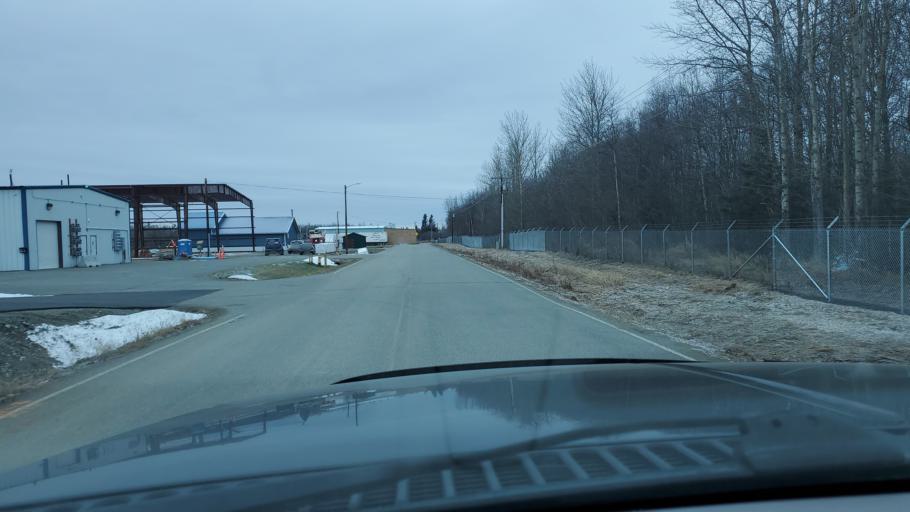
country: US
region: Alaska
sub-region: Matanuska-Susitna Borough
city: Palmer
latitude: 61.5964
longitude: -149.0957
